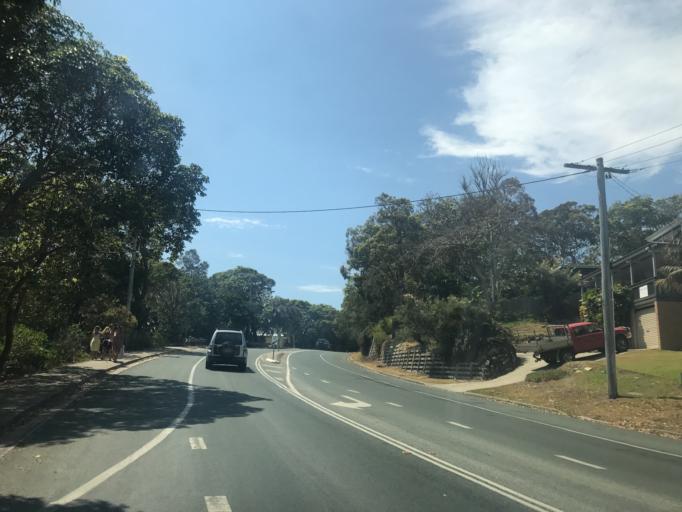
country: AU
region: Queensland
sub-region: Redland
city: Victoria Point
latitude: -27.4271
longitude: 153.5344
